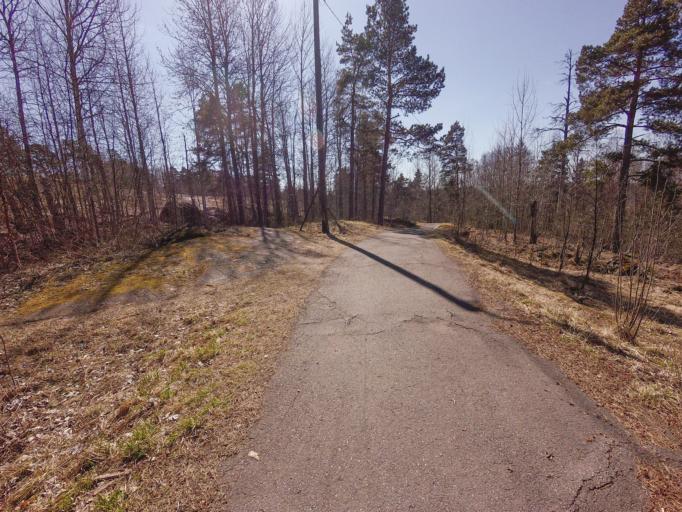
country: FI
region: Uusimaa
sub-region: Helsinki
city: Vantaa
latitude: 60.2019
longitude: 25.0280
